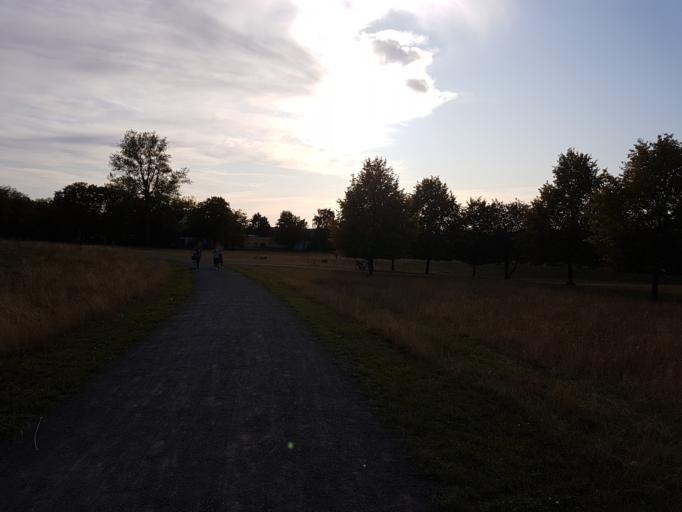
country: DE
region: Lower Saxony
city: Laatzen
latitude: 52.3364
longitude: 9.8422
